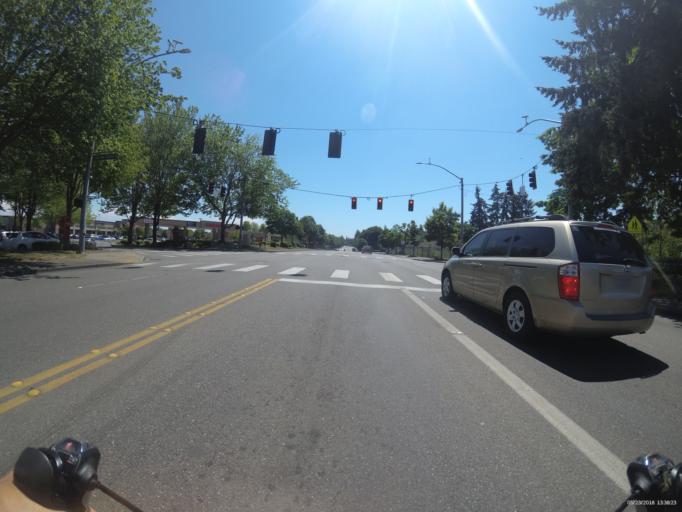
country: US
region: Washington
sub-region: Pierce County
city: Lakewood
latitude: 47.1662
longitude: -122.5206
